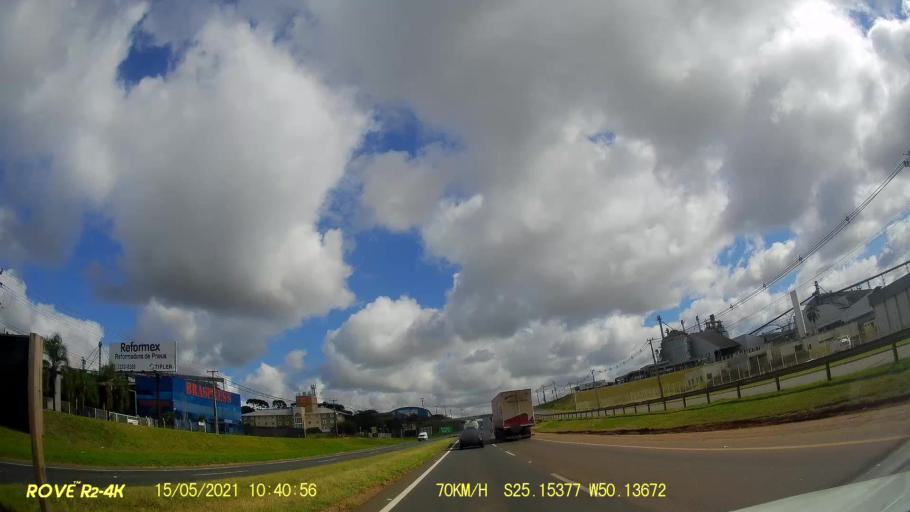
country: BR
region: Parana
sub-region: Ponta Grossa
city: Ponta Grossa
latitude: -25.1528
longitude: -50.1368
